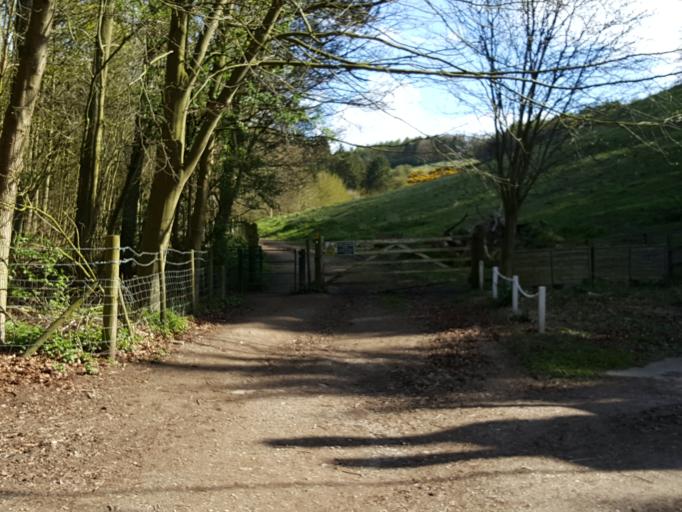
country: GB
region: England
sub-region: East Riding of Yorkshire
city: Welton
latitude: 53.7391
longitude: -0.5431
